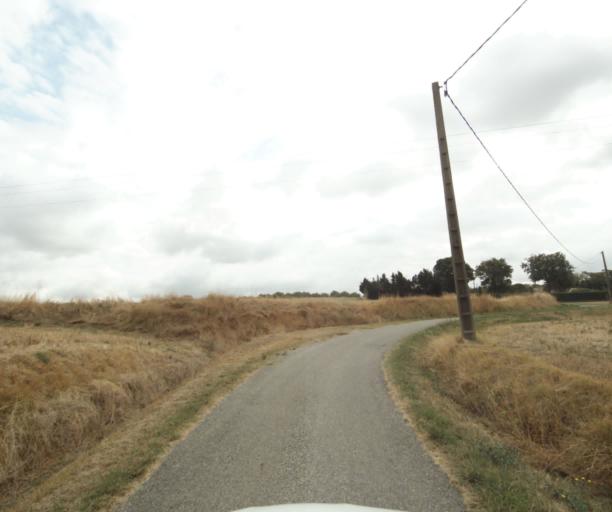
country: FR
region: Midi-Pyrenees
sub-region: Departement de la Haute-Garonne
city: Villefranche-de-Lauragais
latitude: 43.4160
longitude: 1.7119
